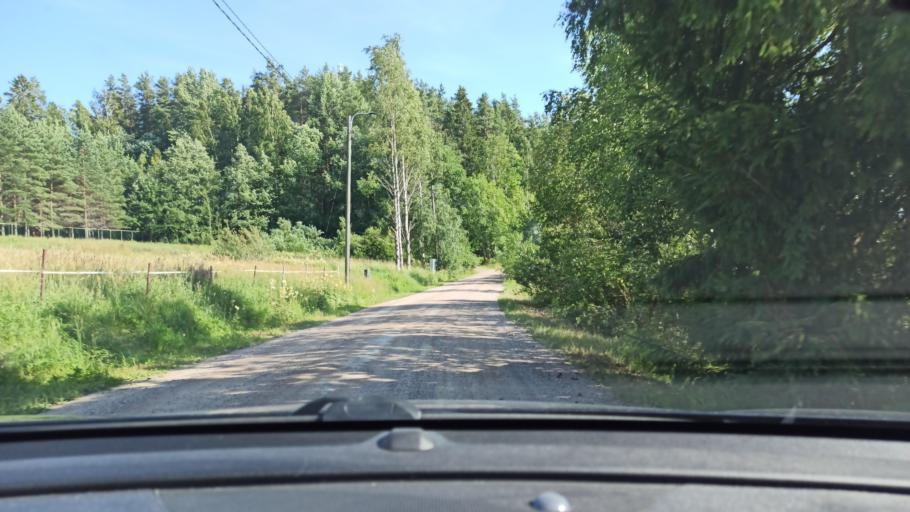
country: FI
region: Uusimaa
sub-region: Helsinki
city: Espoo
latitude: 60.2094
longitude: 24.5546
